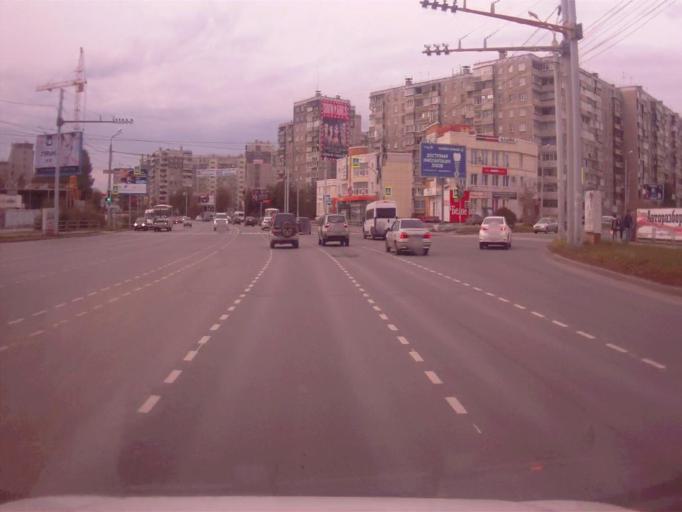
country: RU
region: Chelyabinsk
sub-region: Gorod Chelyabinsk
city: Chelyabinsk
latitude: 55.1781
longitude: 61.3726
